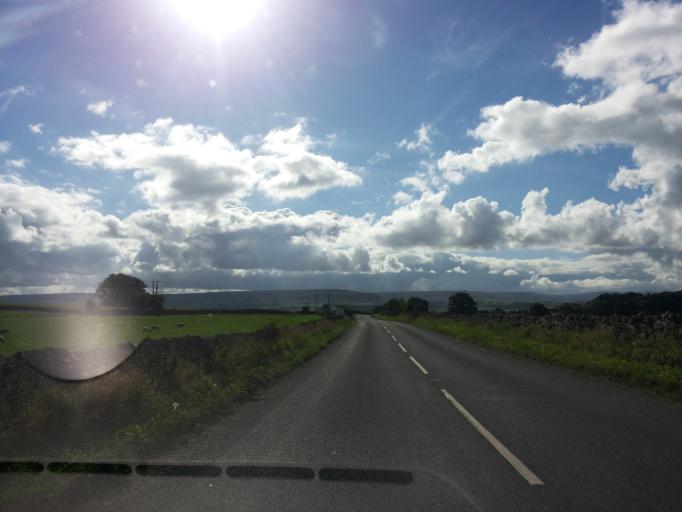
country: GB
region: England
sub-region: North Yorkshire
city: Leyburn
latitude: 54.3201
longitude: -1.8221
